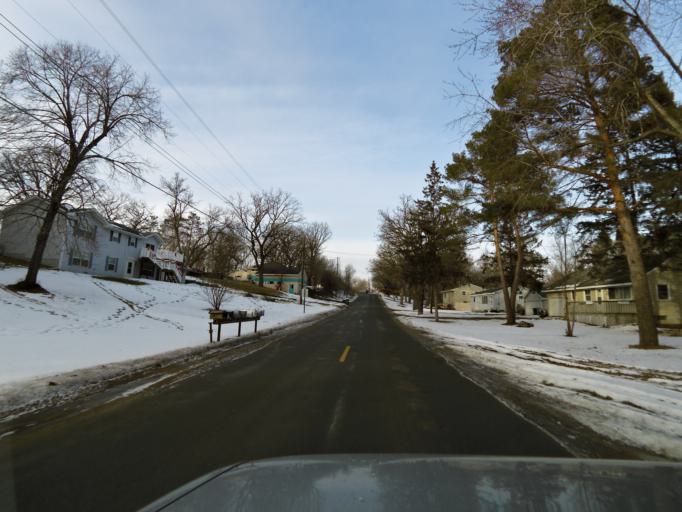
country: US
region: Minnesota
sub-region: Washington County
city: Lake Saint Croix Beach
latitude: 44.9190
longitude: -92.7716
